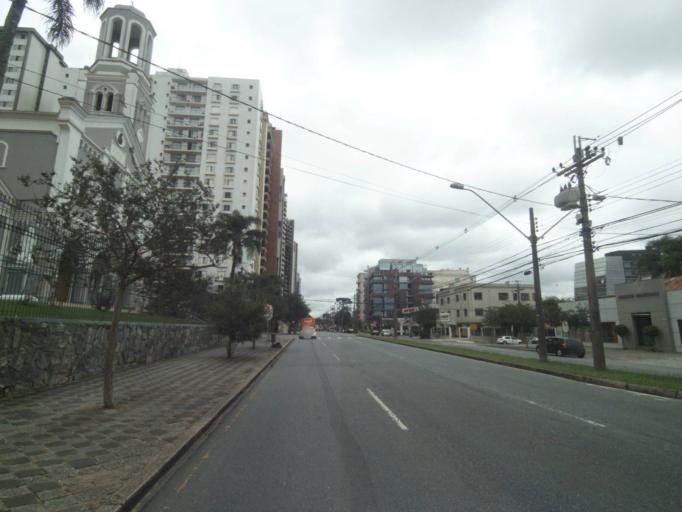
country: BR
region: Parana
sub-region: Curitiba
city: Curitiba
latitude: -25.4439
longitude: -49.2866
